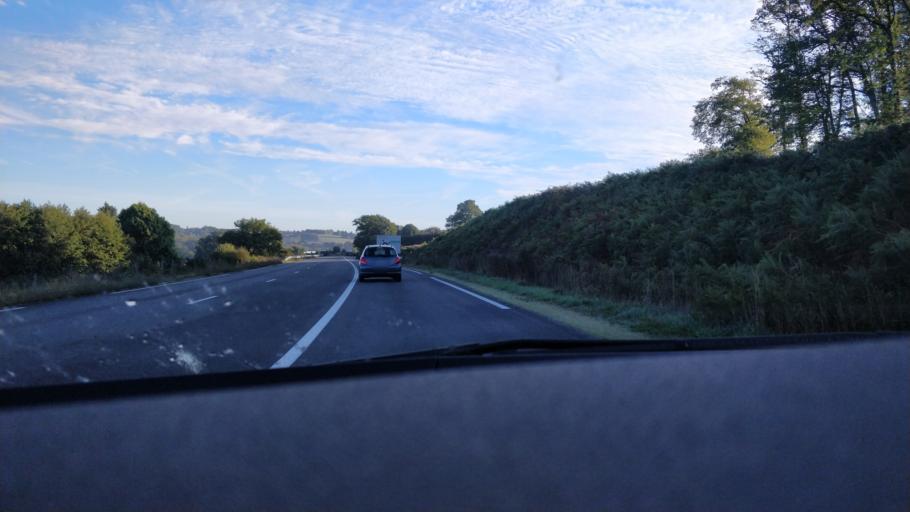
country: FR
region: Limousin
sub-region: Departement de la Creuse
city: Bourganeuf
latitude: 45.9565
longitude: 1.7347
